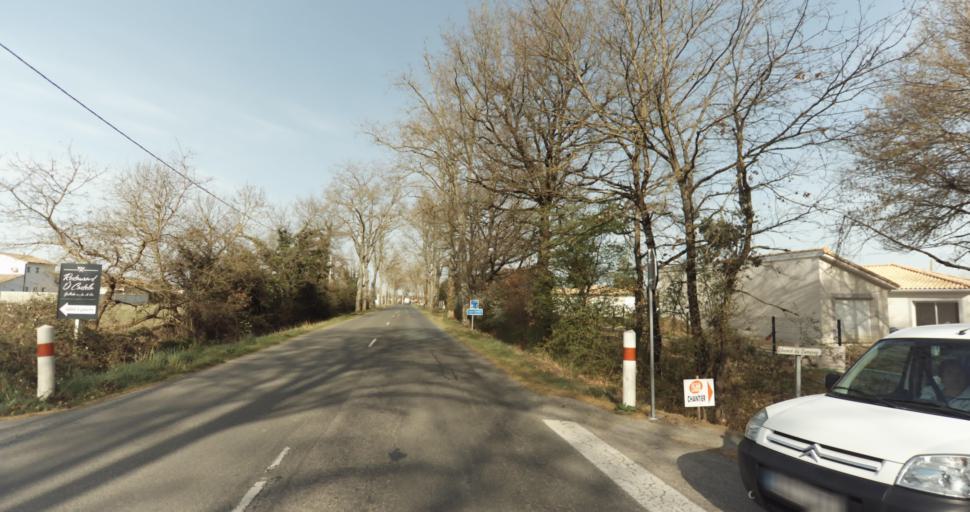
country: FR
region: Midi-Pyrenees
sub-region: Departement du Tarn
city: Saint-Sulpice-la-Pointe
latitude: 43.7604
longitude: 1.7022
